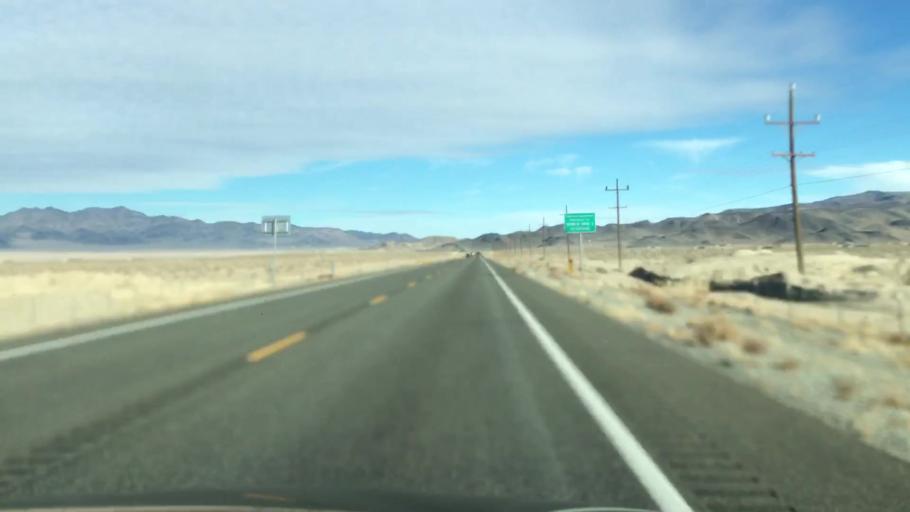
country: US
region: Nevada
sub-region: Mineral County
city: Hawthorne
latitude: 38.5271
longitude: -118.5634
